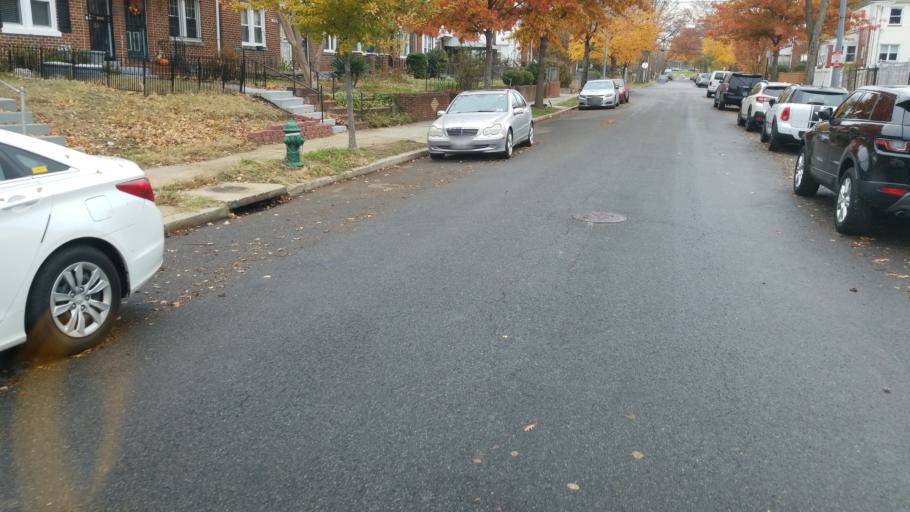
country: US
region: Maryland
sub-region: Prince George's County
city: Colmar Manor
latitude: 38.8936
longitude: -76.9586
